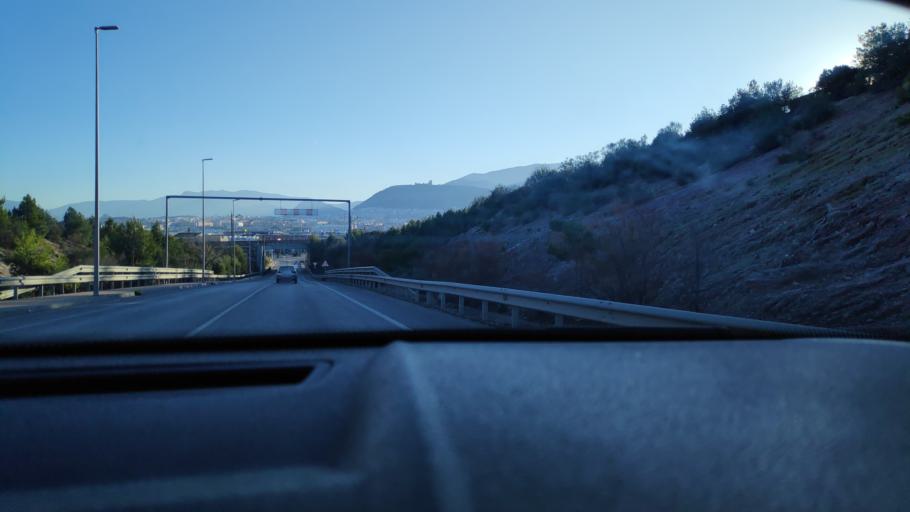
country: ES
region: Andalusia
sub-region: Provincia de Jaen
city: Jaen
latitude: 37.8053
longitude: -3.7881
